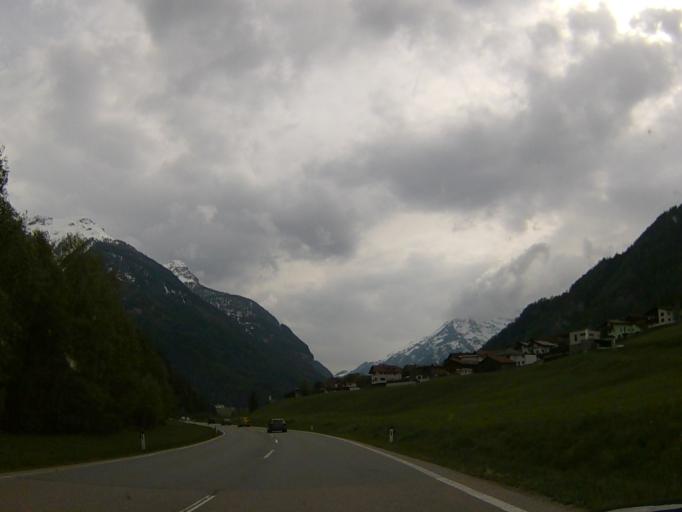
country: AT
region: Tyrol
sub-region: Politischer Bezirk Landeck
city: Pfunds
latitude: 46.9852
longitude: 10.5640
